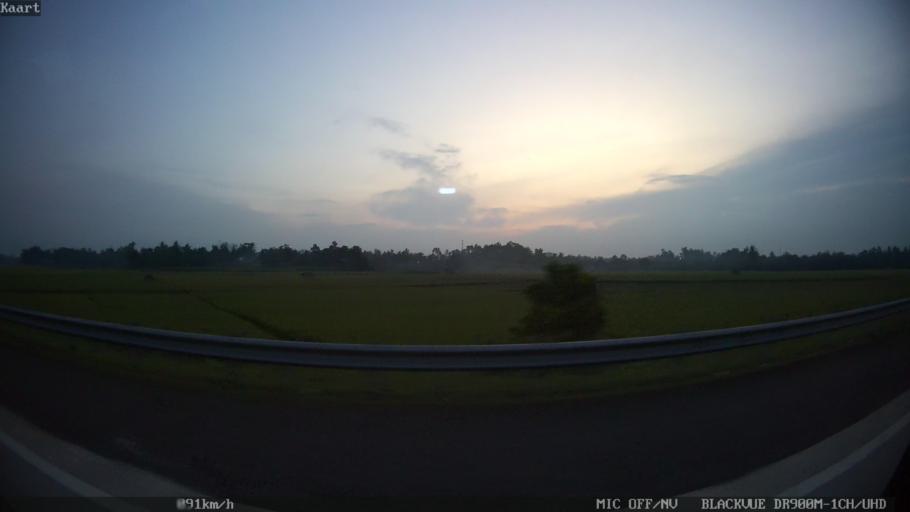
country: ID
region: Lampung
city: Sidorejo
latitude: -5.5745
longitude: 105.5398
